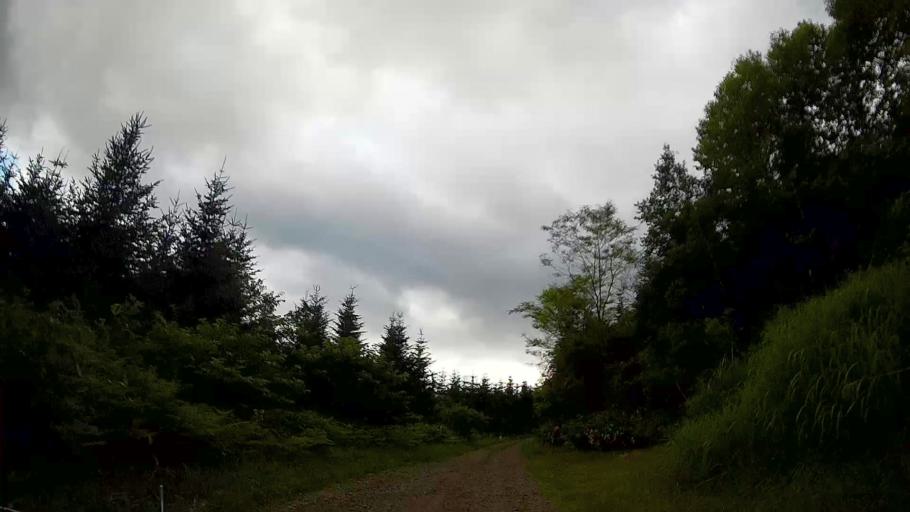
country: JP
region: Hokkaido
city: Nanae
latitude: 42.1259
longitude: 140.4254
